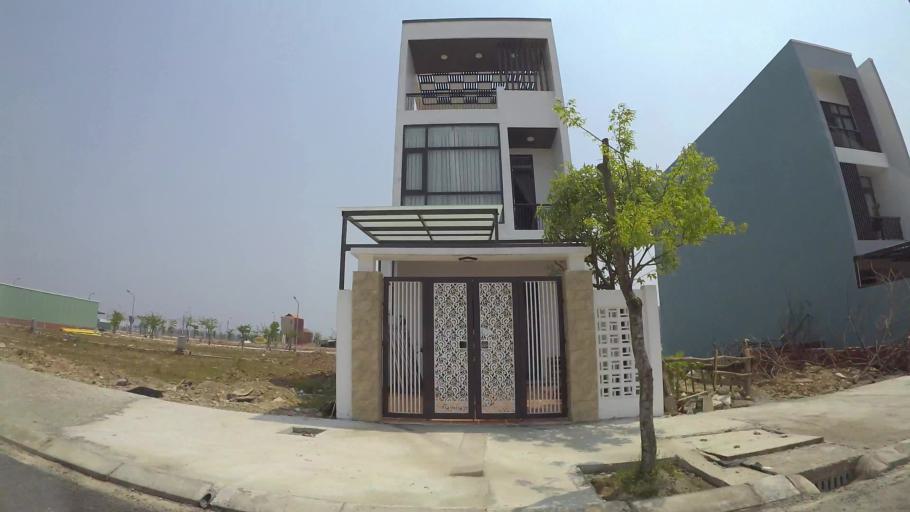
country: VN
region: Da Nang
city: Ngu Hanh Son
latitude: 16.0132
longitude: 108.2405
